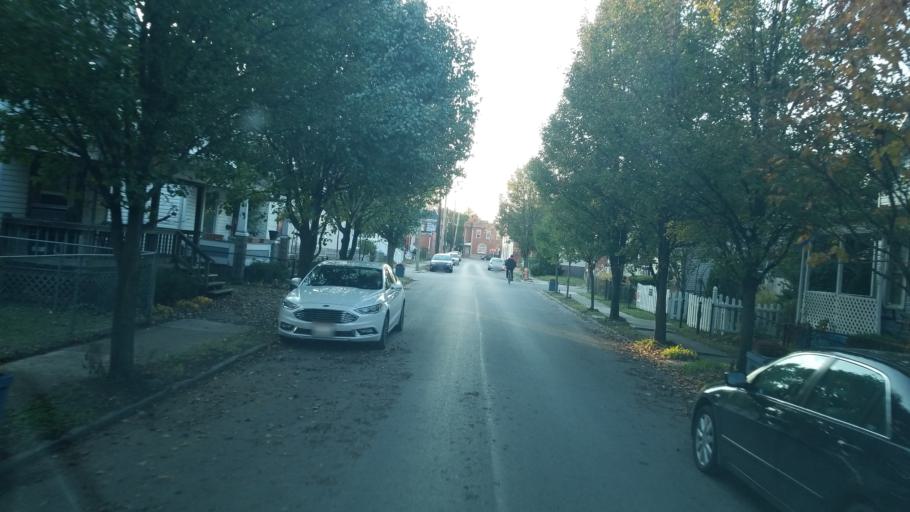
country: US
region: Ohio
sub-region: Franklin County
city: Columbus
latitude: 39.9433
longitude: -82.9812
